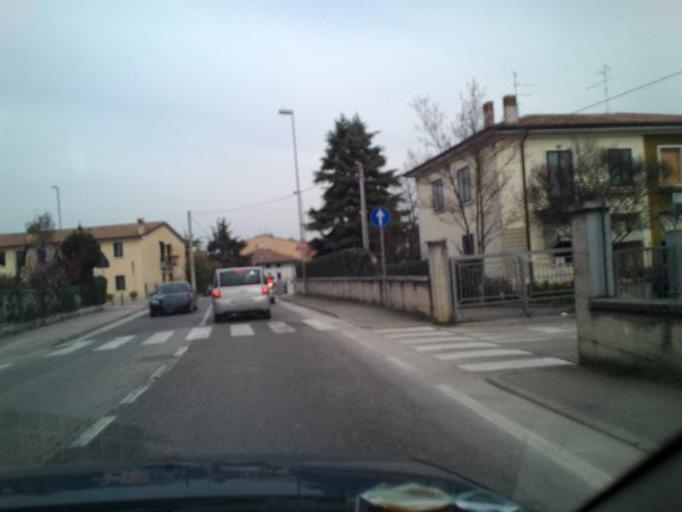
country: IT
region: Veneto
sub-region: Provincia di Verona
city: Villafranca di Verona
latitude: 45.3463
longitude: 10.8439
